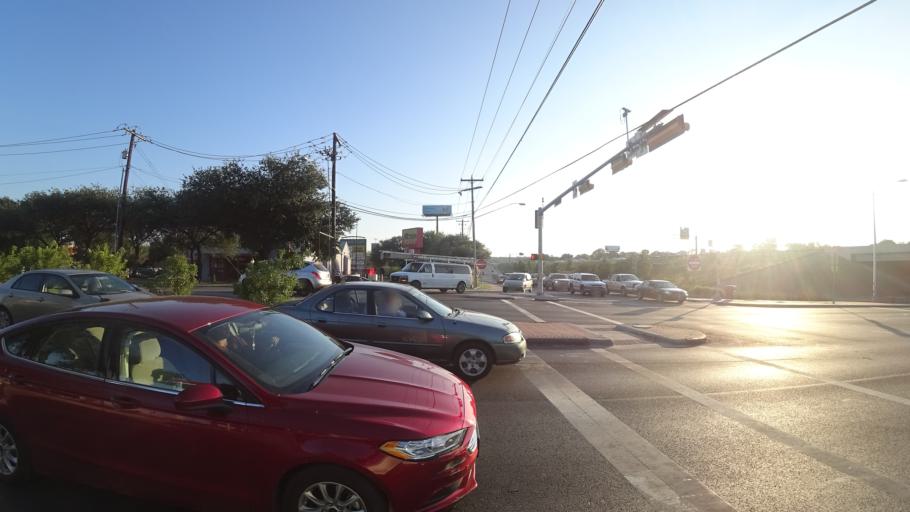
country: US
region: Texas
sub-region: Travis County
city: Wells Branch
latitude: 30.3579
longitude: -97.6873
